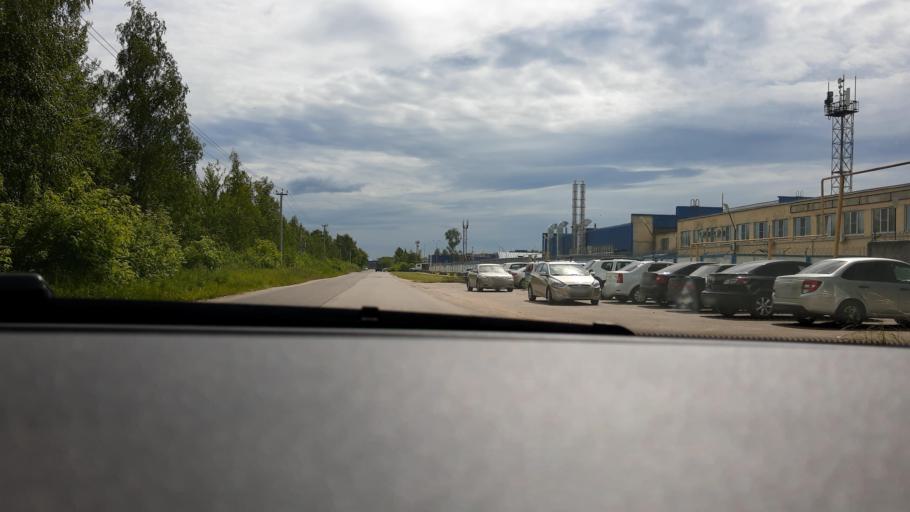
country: RU
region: Nizjnij Novgorod
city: Gorbatovka
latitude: 56.2528
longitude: 43.8077
